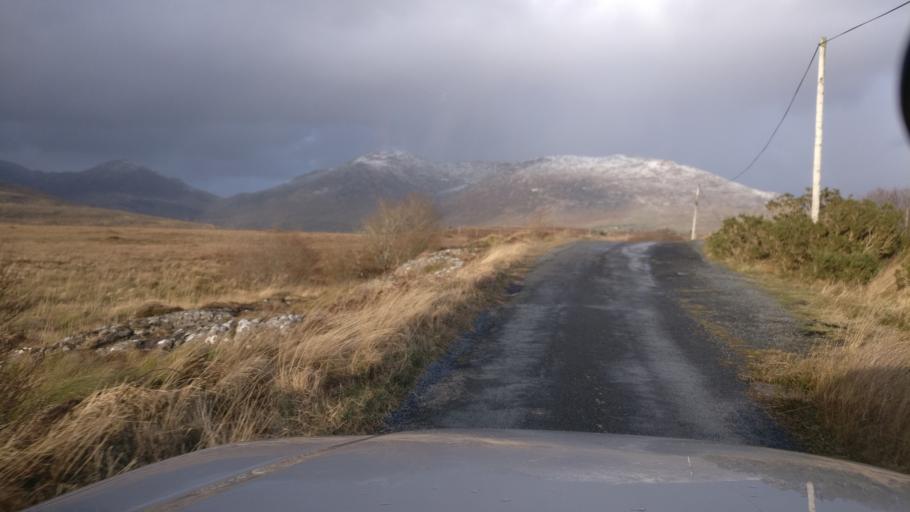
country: IE
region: Connaught
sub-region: County Galway
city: Clifden
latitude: 53.4670
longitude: -9.6965
